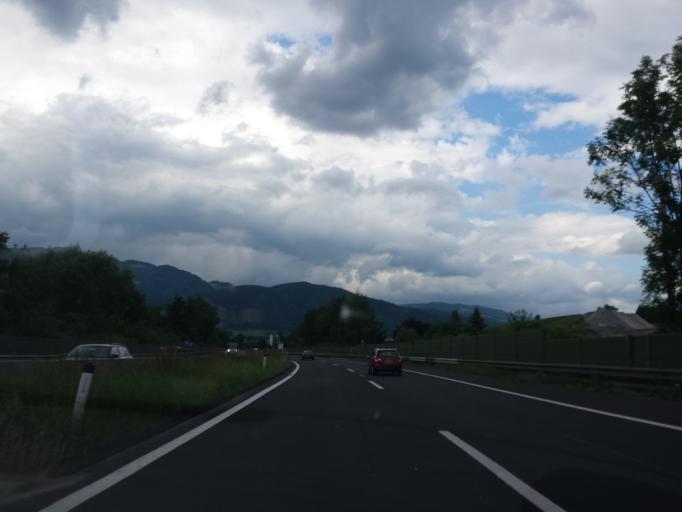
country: AT
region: Styria
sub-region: Politischer Bezirk Bruck-Muerzzuschlag
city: Sankt Marein im Muerztal
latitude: 47.4556
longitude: 15.3445
